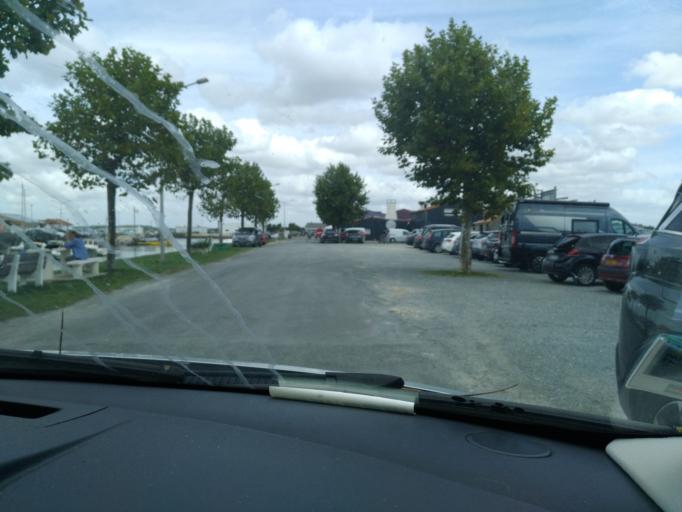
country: FR
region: Poitou-Charentes
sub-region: Departement de la Charente-Maritime
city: Le Gua
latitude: 45.7091
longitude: -0.9766
